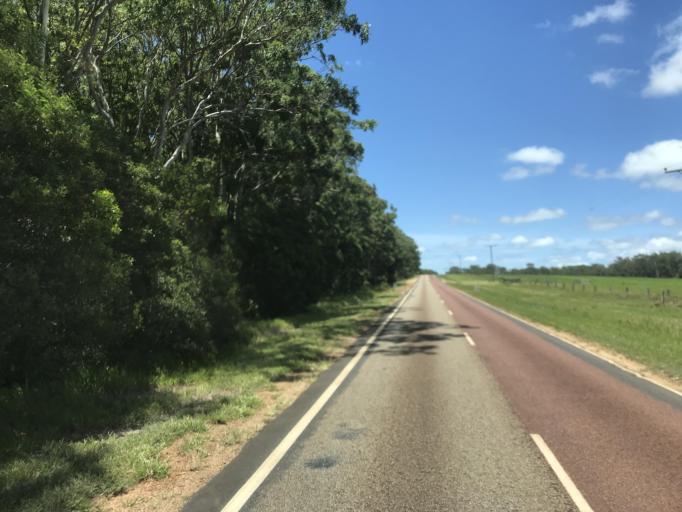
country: AU
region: Queensland
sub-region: Tablelands
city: Ravenshoe
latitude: -17.5245
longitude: 145.4531
